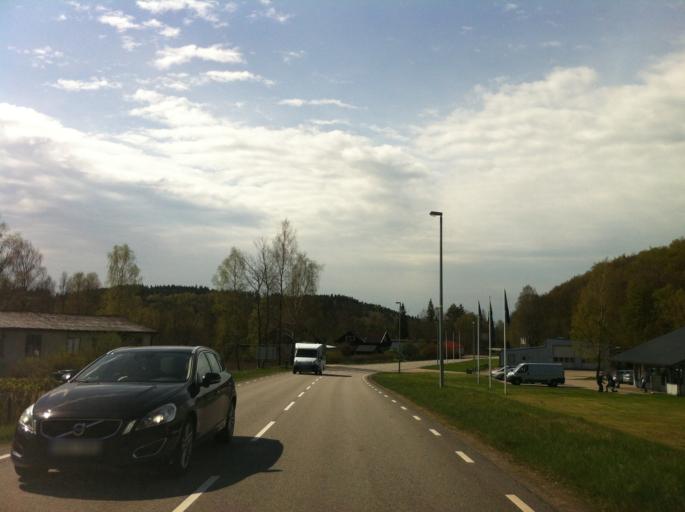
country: SE
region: Vaestra Goetaland
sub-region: Marks Kommun
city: Horred
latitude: 57.1638
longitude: 12.7459
